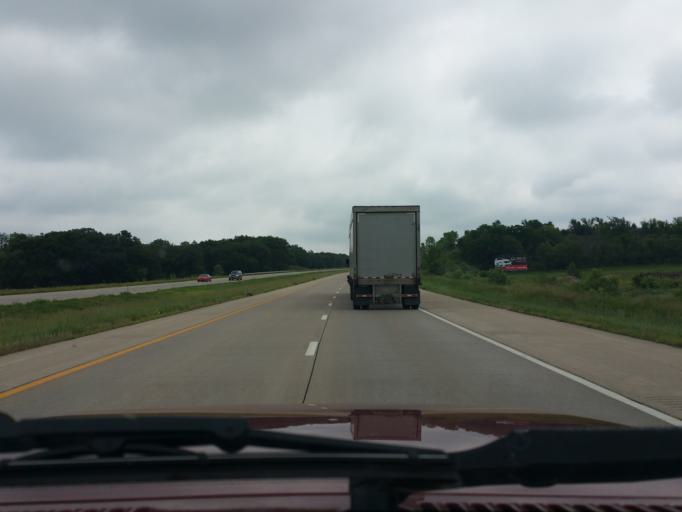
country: US
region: Kansas
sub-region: Shawnee County
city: Silver Lake
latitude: 39.0565
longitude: -95.8435
